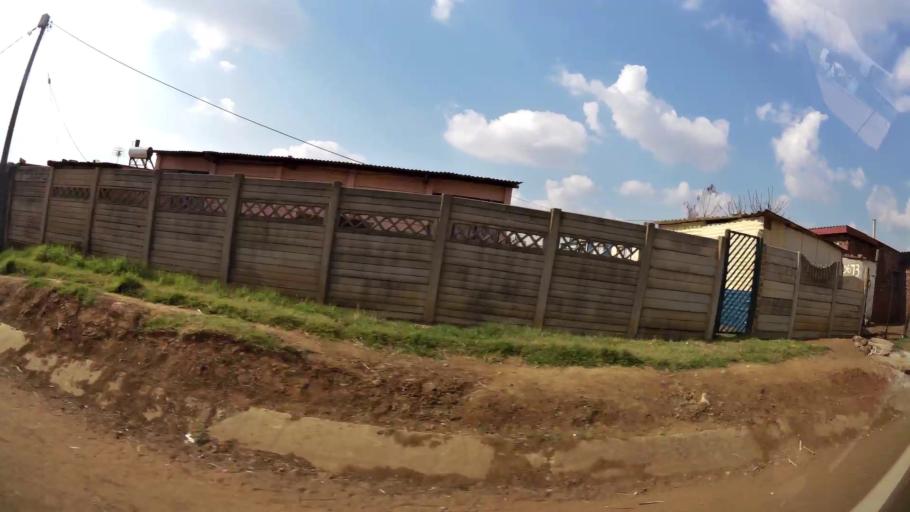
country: ZA
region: Gauteng
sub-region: Ekurhuleni Metropolitan Municipality
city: Springs
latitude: -26.1292
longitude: 28.4766
